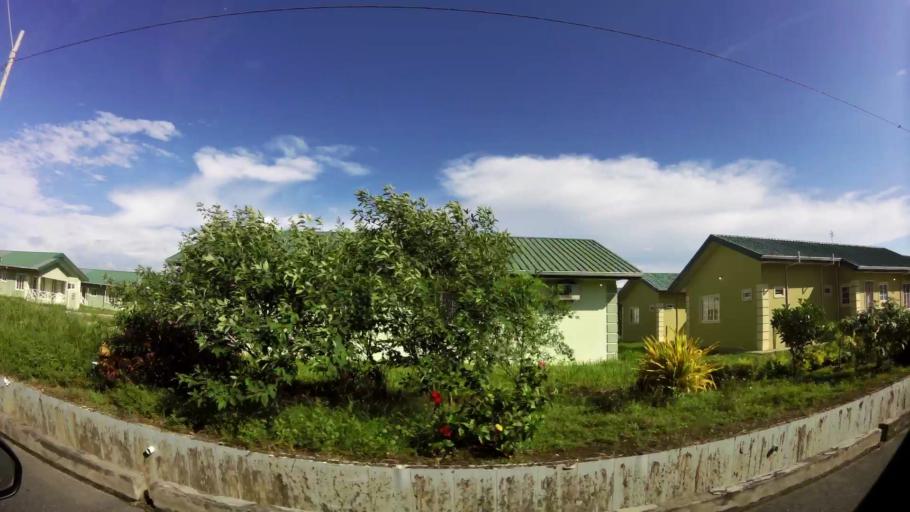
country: TT
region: Chaguanas
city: Chaguanas
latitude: 10.5305
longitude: -61.3926
